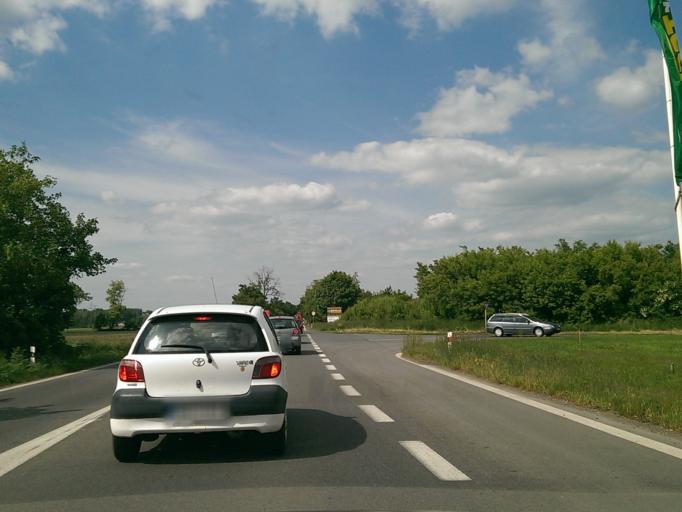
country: CZ
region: Central Bohemia
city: Libis
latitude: 50.2820
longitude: 14.4958
